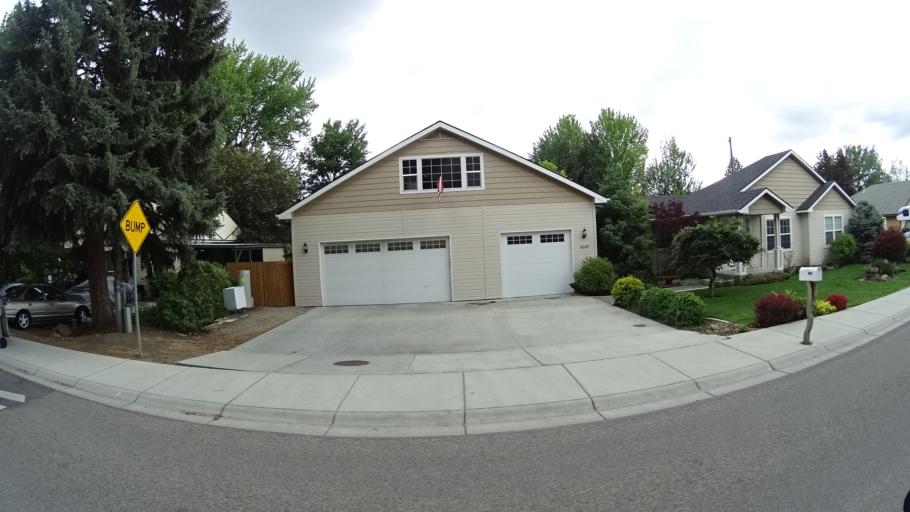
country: US
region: Idaho
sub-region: Ada County
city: Garden City
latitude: 43.6555
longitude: -116.2413
